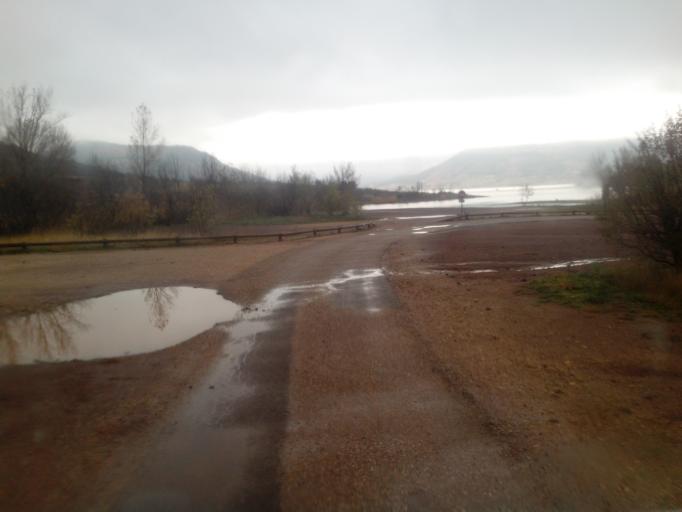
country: FR
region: Languedoc-Roussillon
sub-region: Departement de l'Herault
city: Lodeve
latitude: 43.6482
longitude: 3.3504
